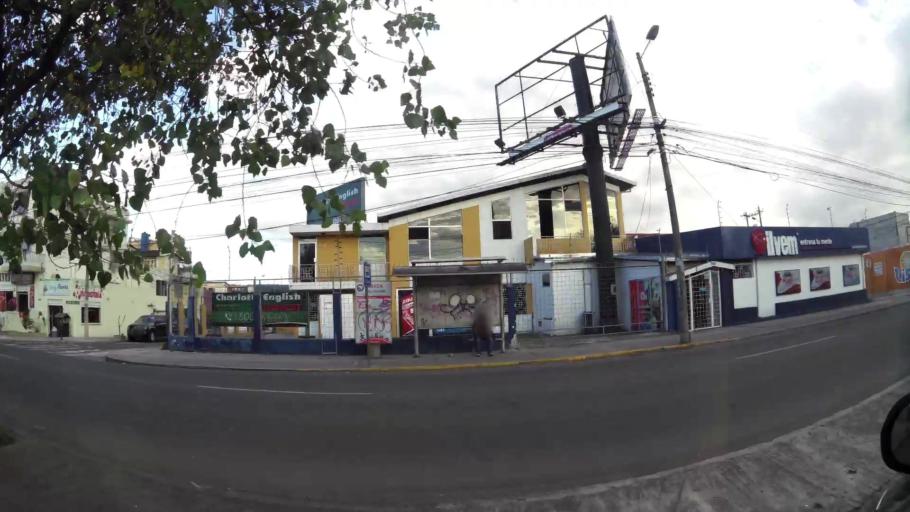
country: EC
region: Pichincha
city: Quito
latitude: -0.1586
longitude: -78.4831
